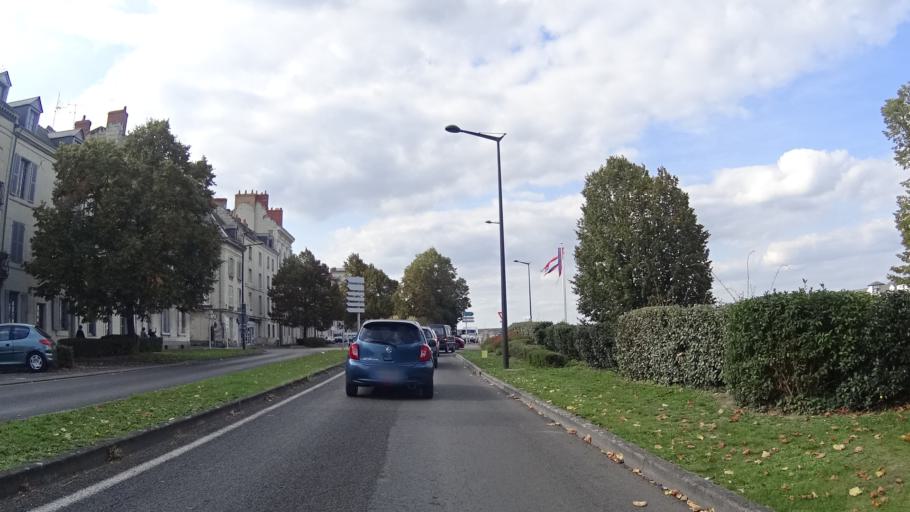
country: FR
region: Pays de la Loire
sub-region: Departement de Maine-et-Loire
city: Saumur
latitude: 47.2587
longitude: -0.0721
